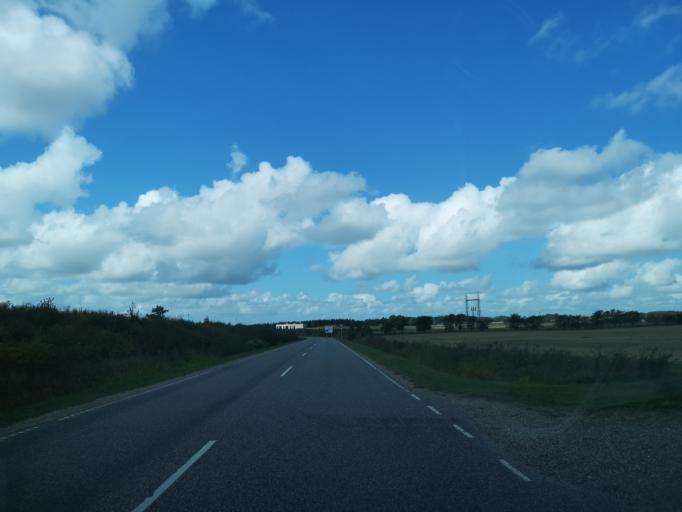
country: DK
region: Central Jutland
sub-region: Holstebro Kommune
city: Holstebro
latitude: 56.3909
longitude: 8.5892
